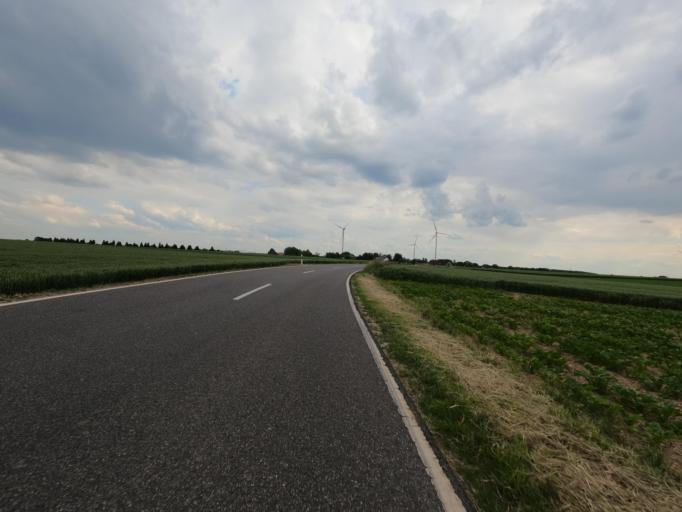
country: DE
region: North Rhine-Westphalia
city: Huckelhoven
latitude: 51.0764
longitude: 6.2516
